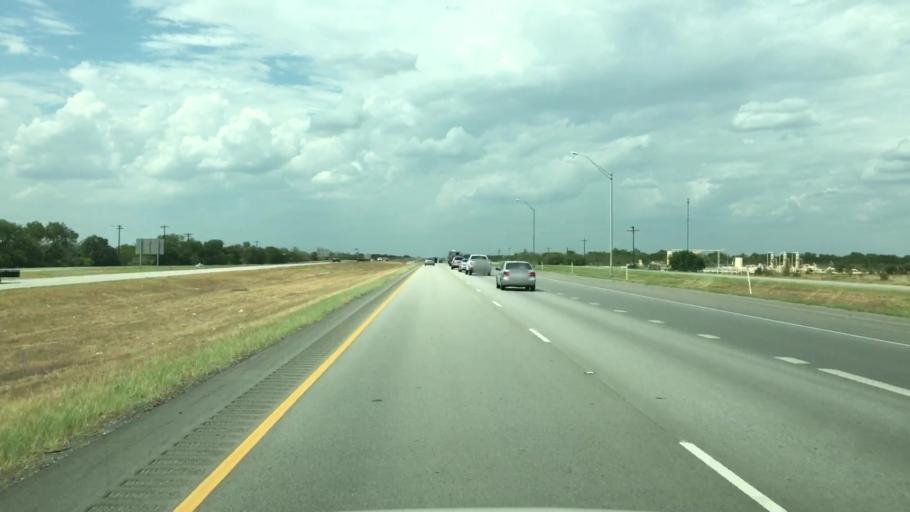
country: US
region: Texas
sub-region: Live Oak County
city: Three Rivers
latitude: 28.5350
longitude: -98.1889
